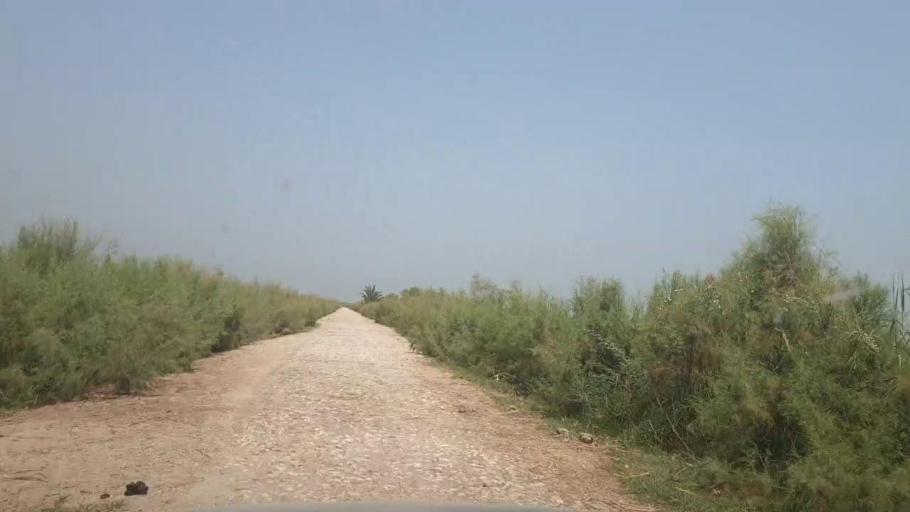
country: PK
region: Sindh
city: Lakhi
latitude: 27.8402
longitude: 68.6264
